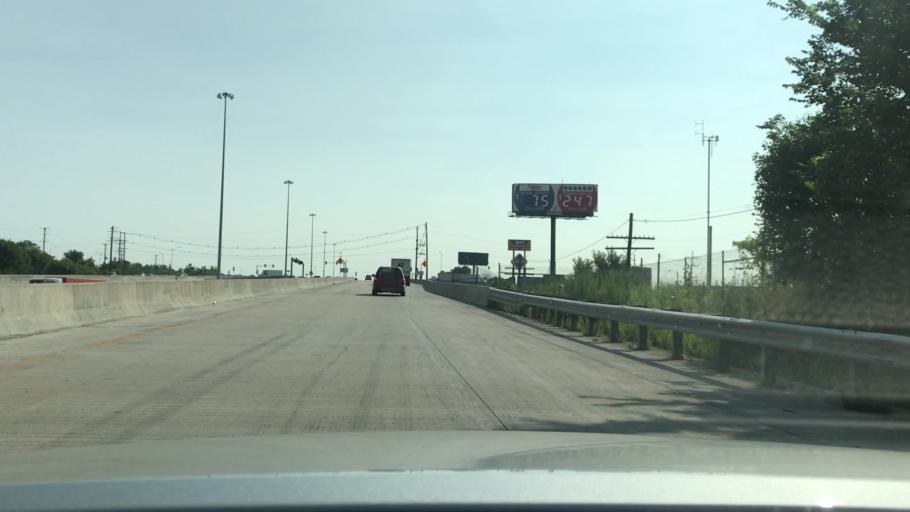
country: US
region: Illinois
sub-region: Cook County
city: Stickney
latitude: 41.8095
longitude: -87.7665
